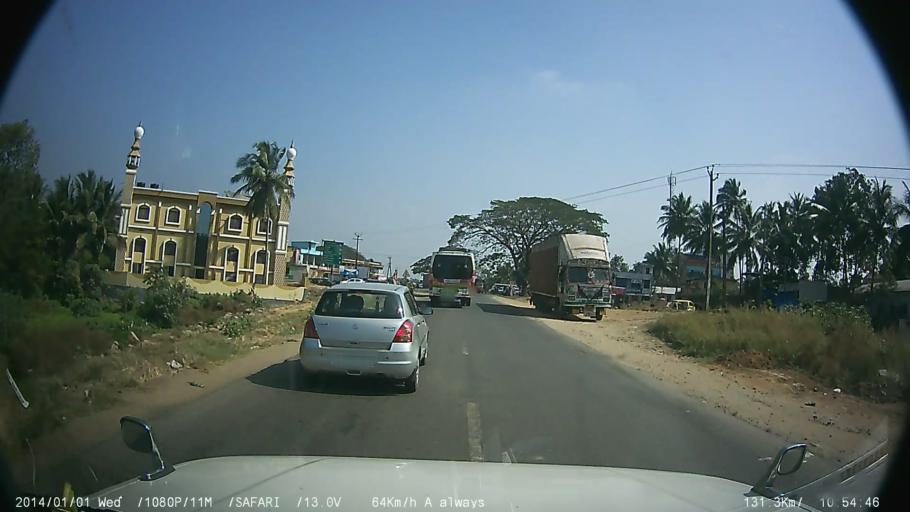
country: IN
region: Kerala
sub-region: Palakkad district
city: Palakkad
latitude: 10.7185
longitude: 76.6002
